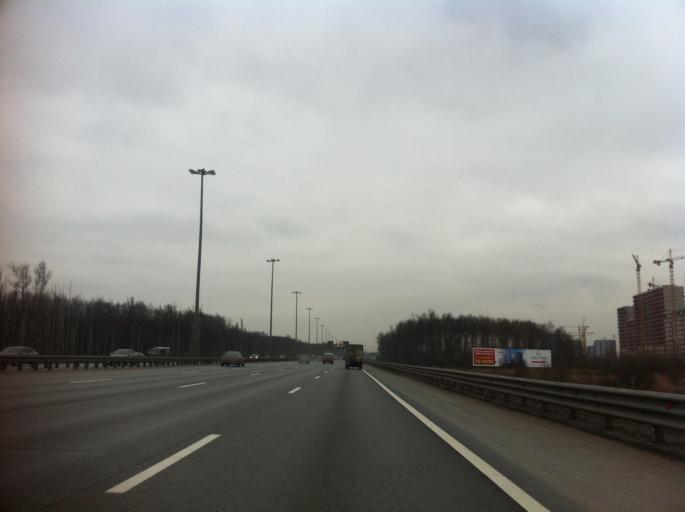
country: RU
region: Leningrad
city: Rybatskoye
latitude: 59.9095
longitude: 30.5258
